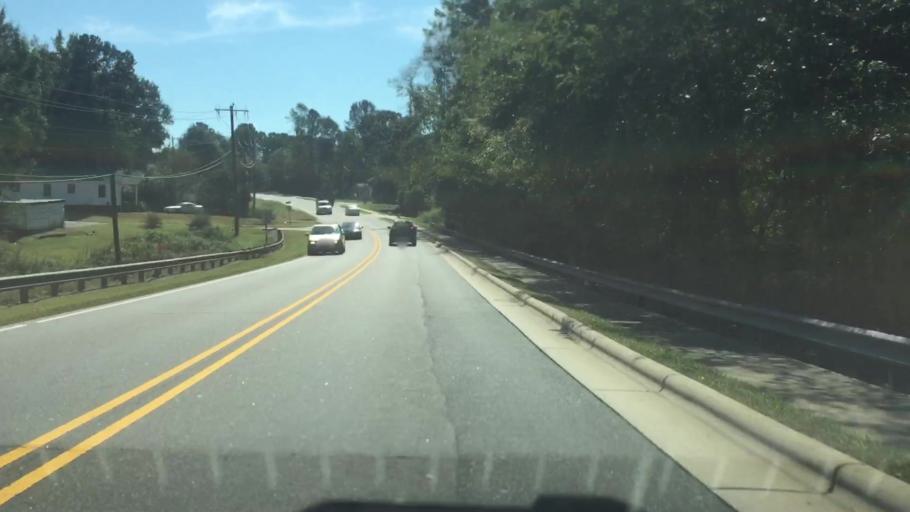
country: US
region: North Carolina
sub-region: Iredell County
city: Mooresville
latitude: 35.5925
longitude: -80.8157
